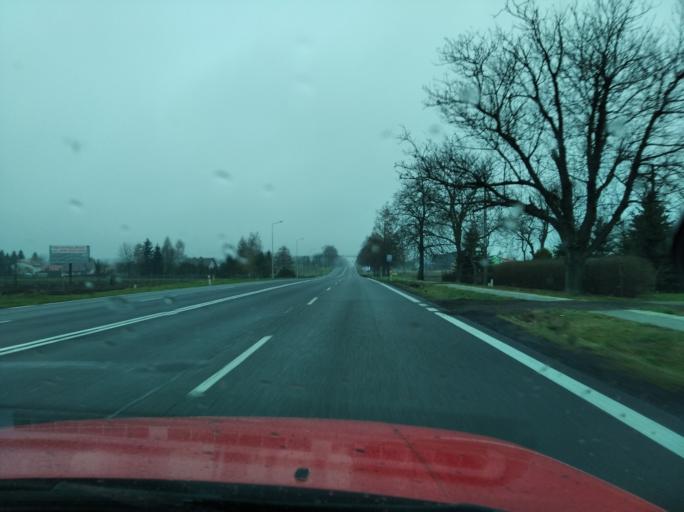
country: PL
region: Subcarpathian Voivodeship
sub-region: Powiat przeworski
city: Grzeska
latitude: 50.0630
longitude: 22.4490
